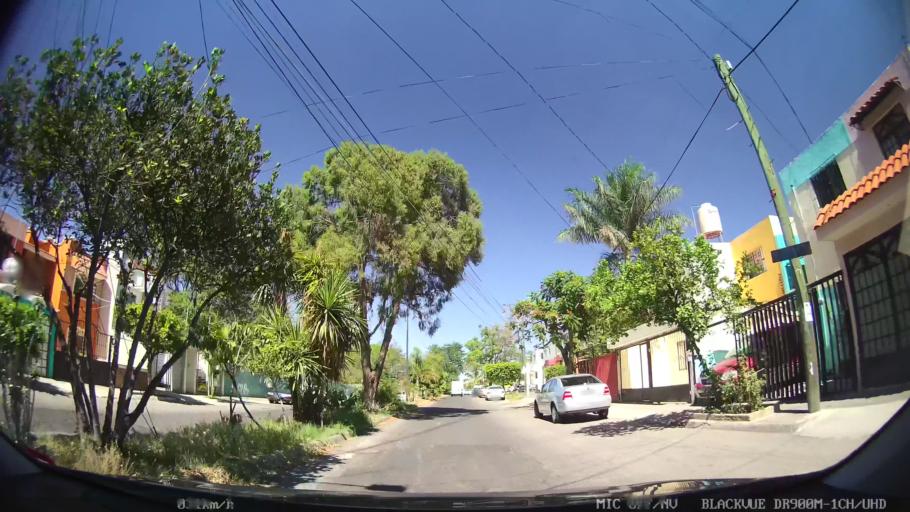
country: MX
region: Jalisco
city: Tlaquepaque
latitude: 20.6479
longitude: -103.2935
